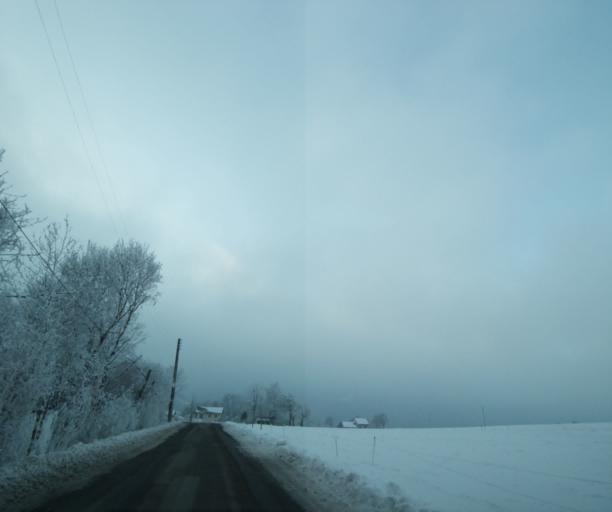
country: FR
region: Rhone-Alpes
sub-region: Departement de la Haute-Savoie
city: Monnetier-Mornex
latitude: 46.1167
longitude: 6.2192
